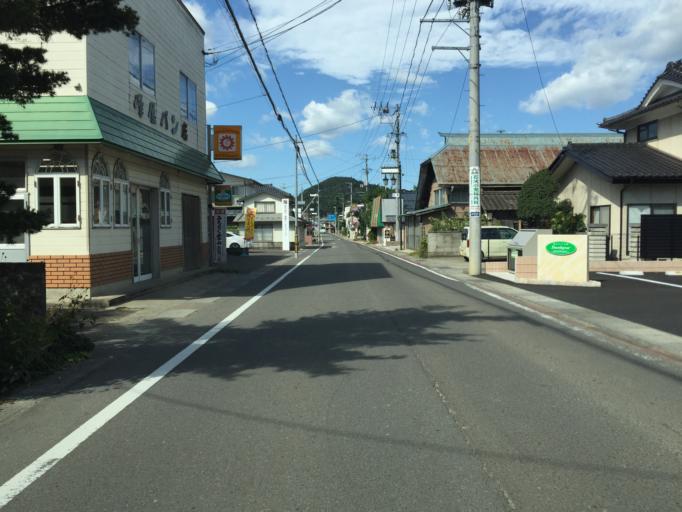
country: JP
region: Fukushima
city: Hobaramachi
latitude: 37.7857
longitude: 140.5944
